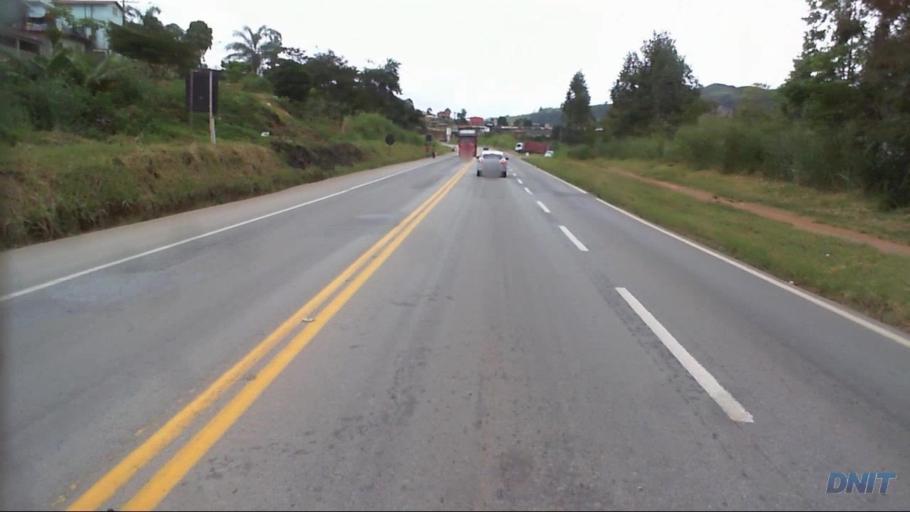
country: BR
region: Minas Gerais
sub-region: Joao Monlevade
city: Joao Monlevade
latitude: -19.8448
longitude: -43.1679
